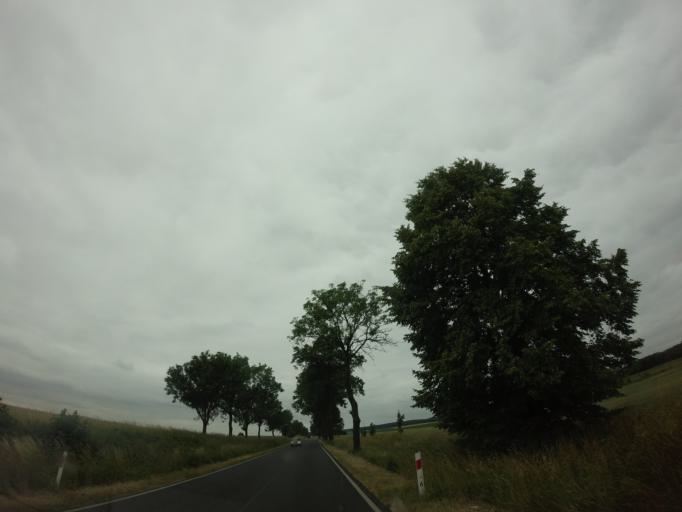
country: PL
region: West Pomeranian Voivodeship
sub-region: Powiat choszczenski
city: Recz
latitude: 53.1886
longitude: 15.5685
